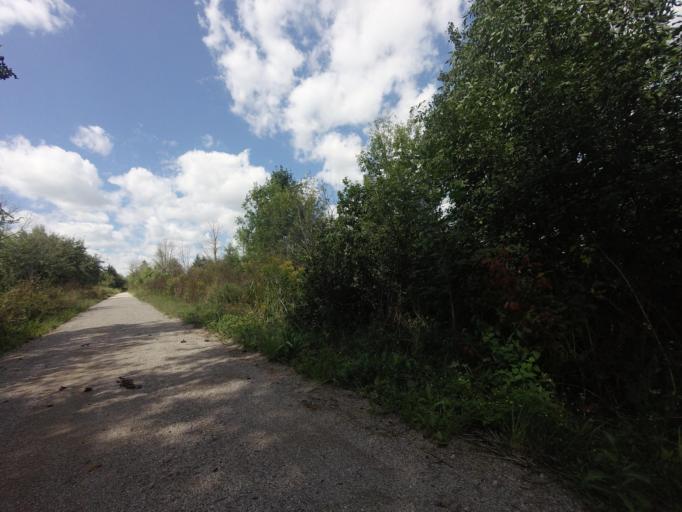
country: CA
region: Ontario
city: Huron East
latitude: 43.6217
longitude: -81.1575
